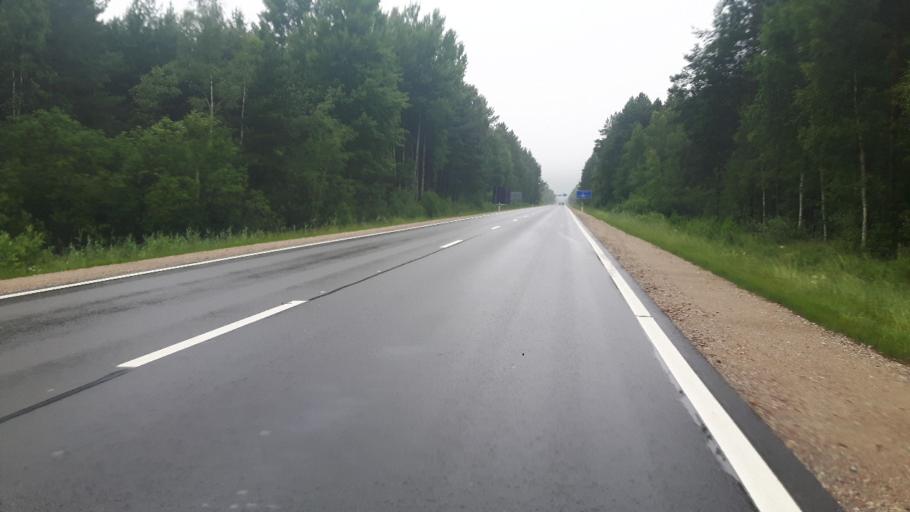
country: LV
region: Rucavas
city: Rucava
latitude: 56.1528
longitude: 21.1487
